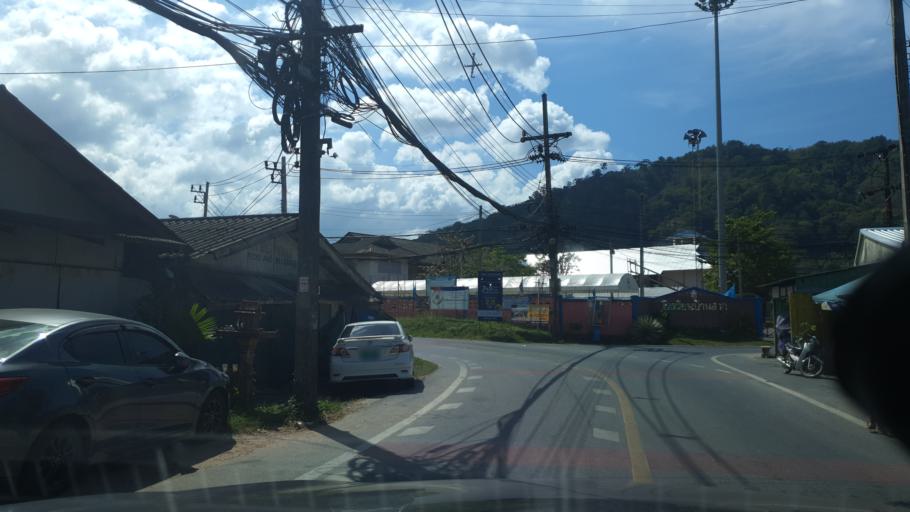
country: TH
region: Phuket
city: Thalang
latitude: 8.0744
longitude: 98.2982
